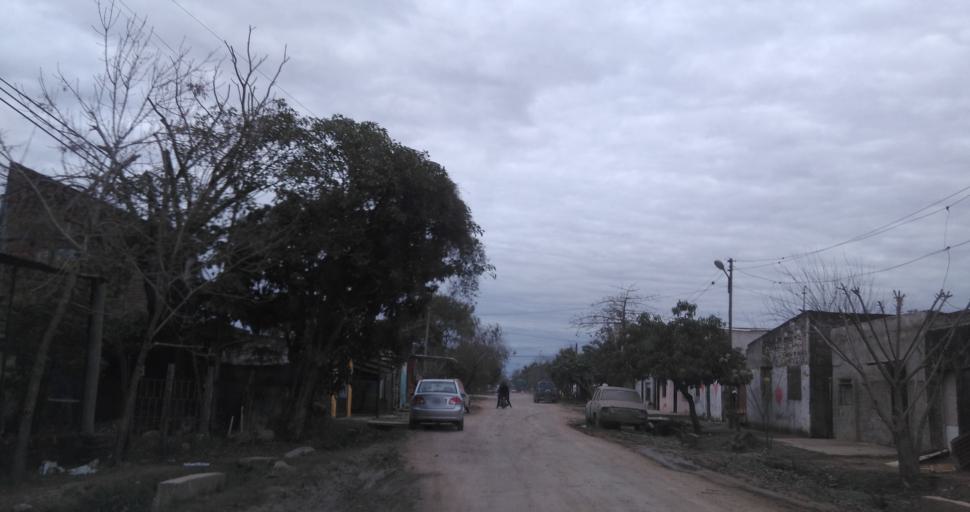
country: AR
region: Chaco
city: Resistencia
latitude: -27.4711
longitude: -58.9676
